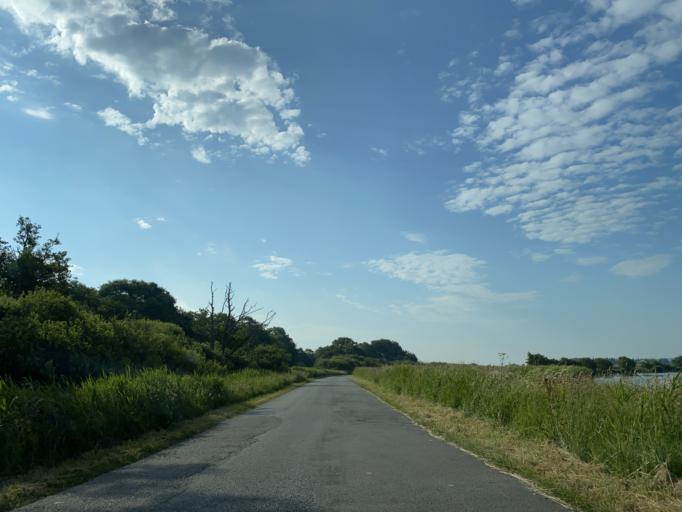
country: DK
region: South Denmark
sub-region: Haderslev Kommune
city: Haderslev
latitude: 55.1700
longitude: 9.4890
